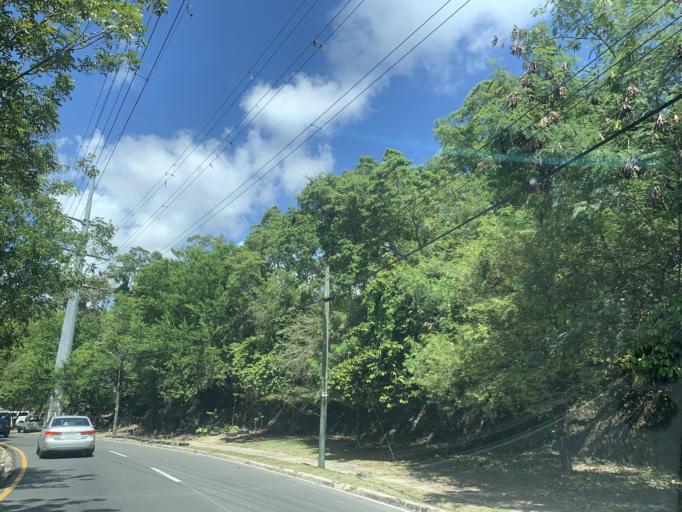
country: DO
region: Nacional
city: La Agustina
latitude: 18.5059
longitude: -69.9277
